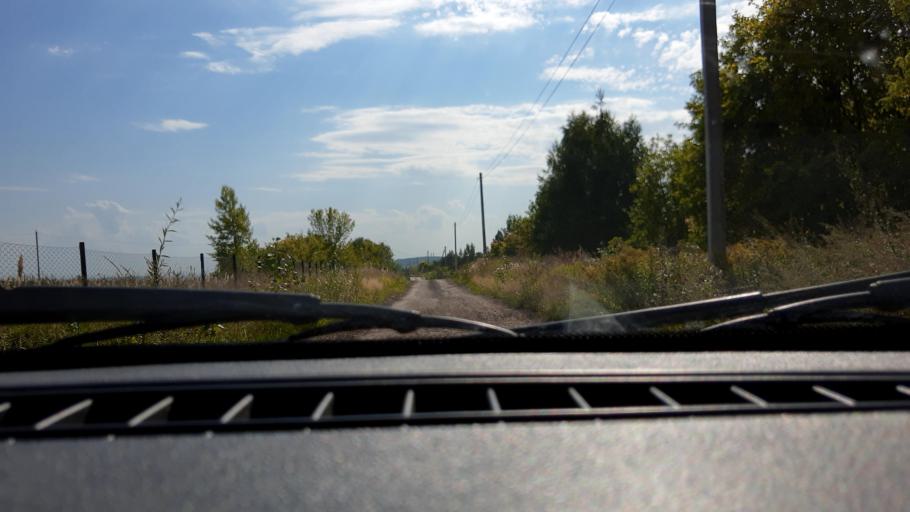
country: RU
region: Bashkortostan
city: Ufa
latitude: 54.8508
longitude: 56.1630
